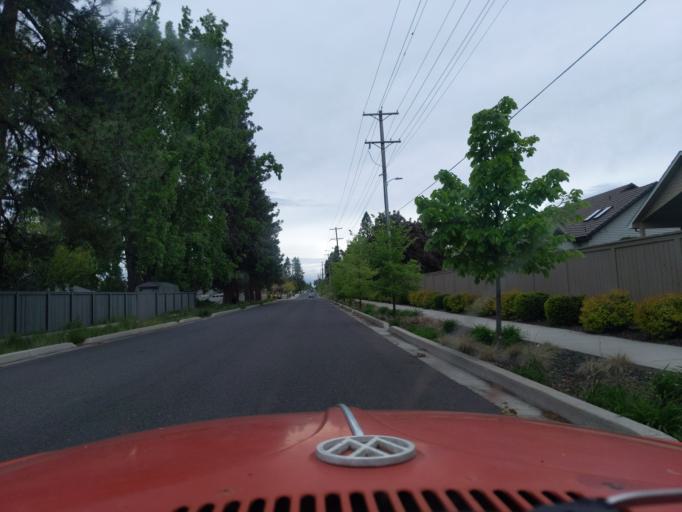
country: US
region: Washington
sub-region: Spokane County
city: Spokane
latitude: 47.6089
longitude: -117.3791
